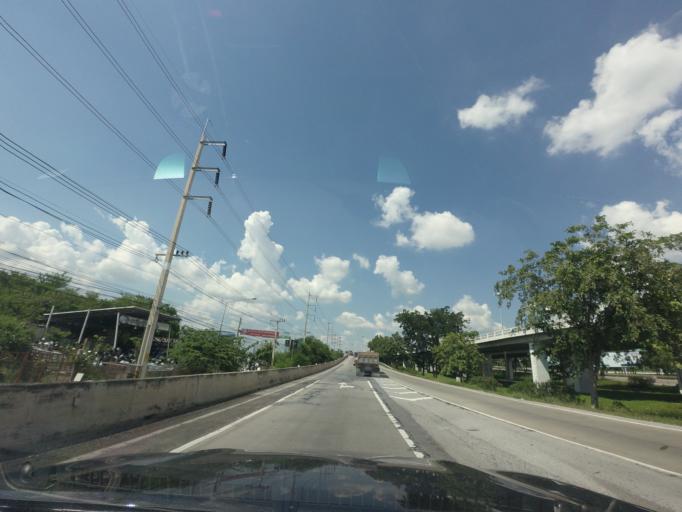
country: TH
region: Nakhon Ratchasima
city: Nakhon Ratchasima
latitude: 14.9623
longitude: 102.0528
